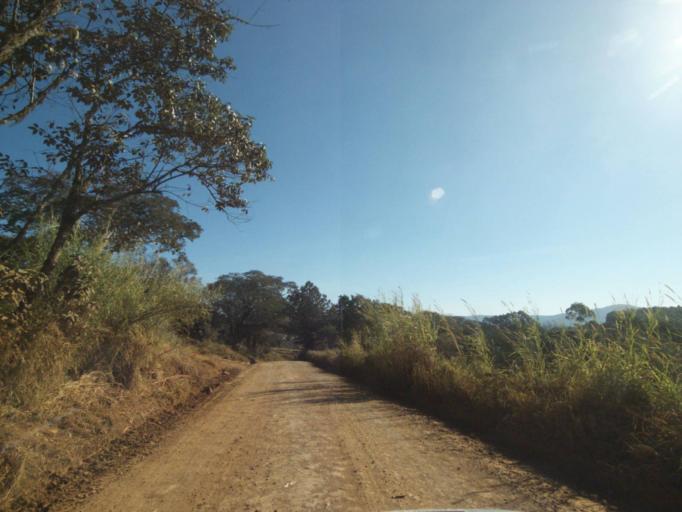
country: BR
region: Parana
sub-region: Tibagi
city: Tibagi
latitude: -24.5392
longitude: -50.4709
